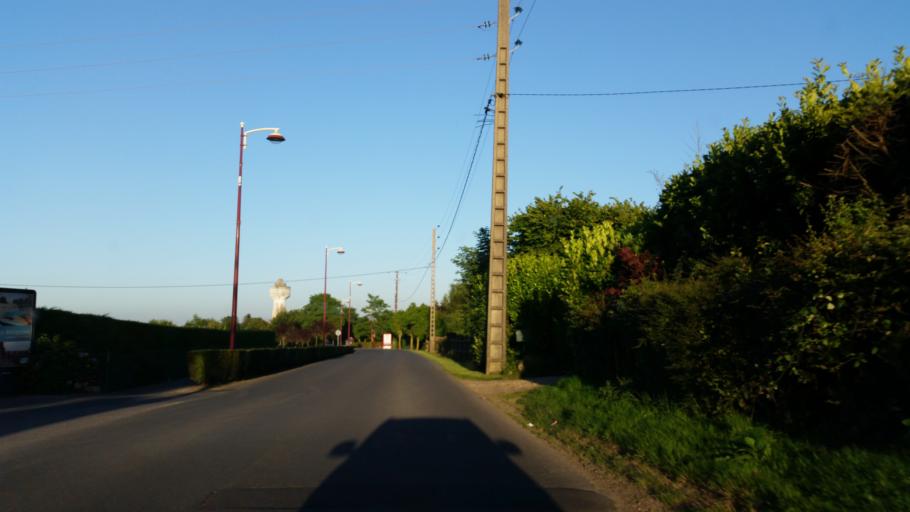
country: FR
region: Lower Normandy
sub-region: Departement du Calvados
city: Equemauville
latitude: 49.3968
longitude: 0.2081
